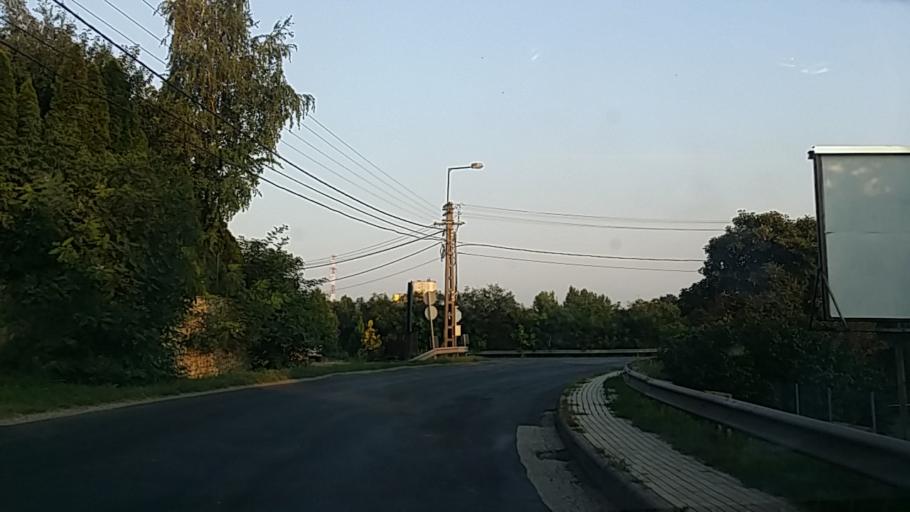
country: HU
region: Fejer
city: dunaujvaros
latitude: 46.9834
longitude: 18.9369
